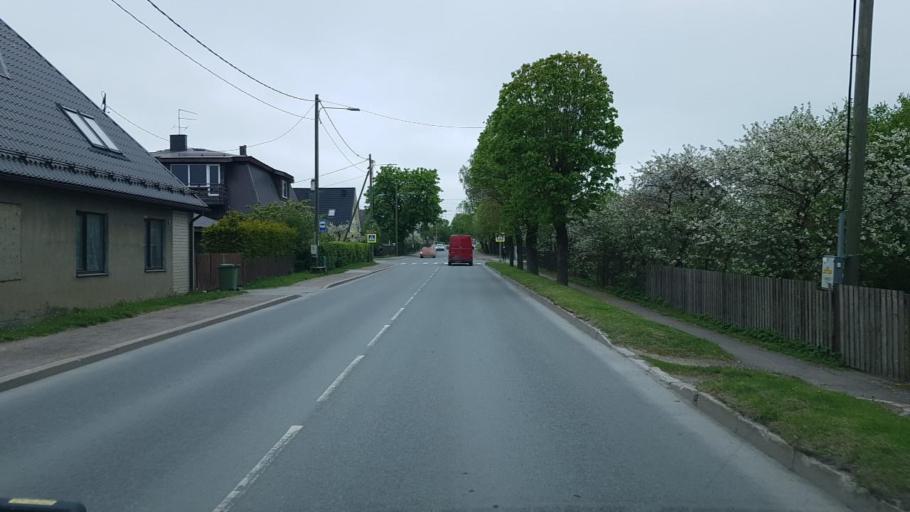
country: EE
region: Harju
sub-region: Keila linn
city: Keila
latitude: 59.3045
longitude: 24.4254
